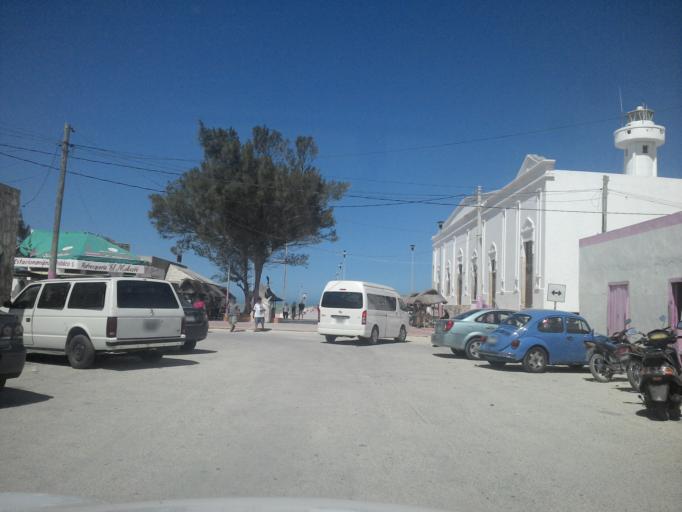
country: MX
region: Yucatan
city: Telchac Puerto
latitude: 21.3433
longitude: -89.2637
